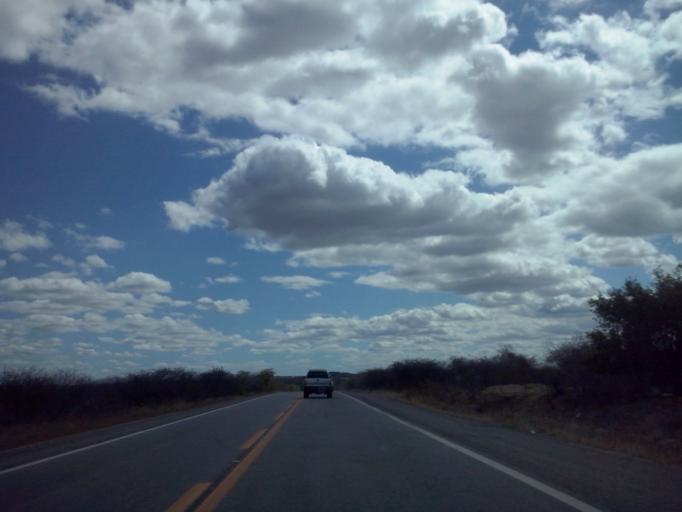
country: BR
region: Paraiba
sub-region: Soledade
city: Soledade
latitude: -7.0384
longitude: -36.4254
